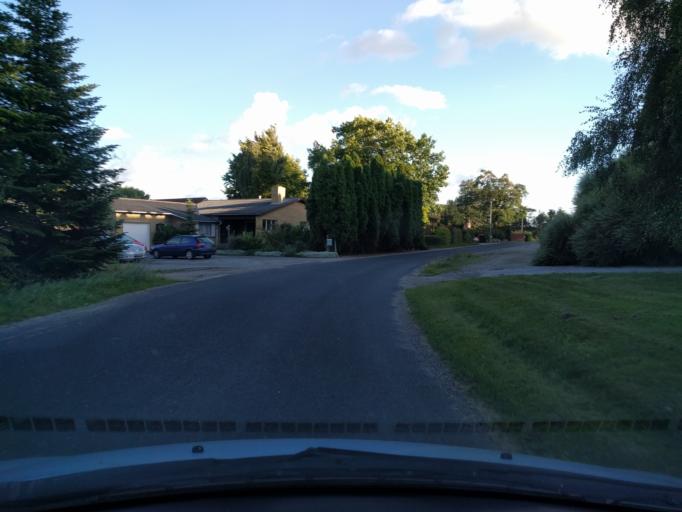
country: DK
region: South Denmark
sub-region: Nyborg Kommune
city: Ullerslev
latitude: 55.3657
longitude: 10.6591
